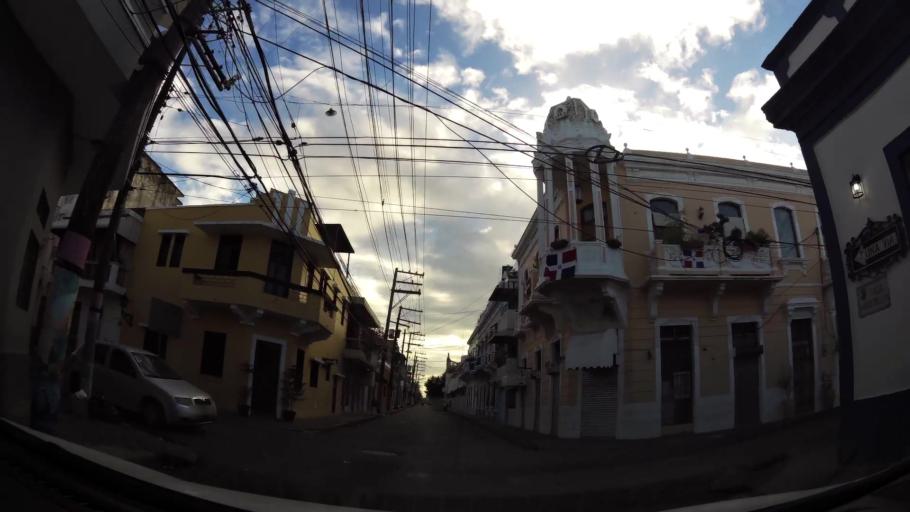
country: DO
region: Nacional
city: Ciudad Nueva
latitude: 18.4704
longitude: -69.8882
